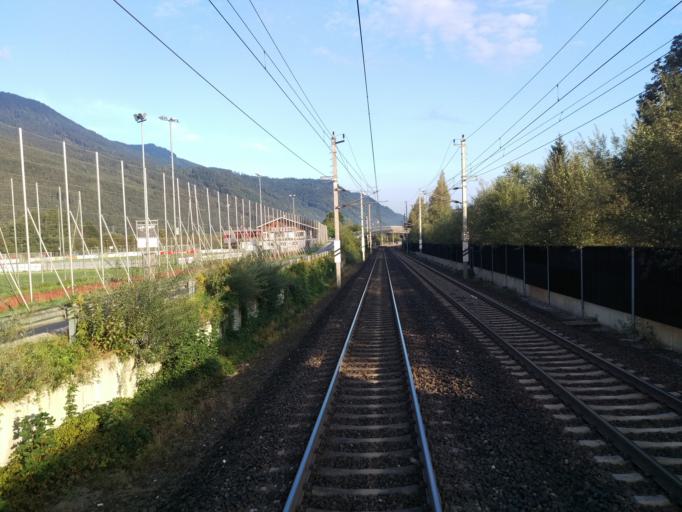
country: AT
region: Salzburg
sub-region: Politischer Bezirk Hallein
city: Kuchl
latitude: 47.6222
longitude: 13.1447
